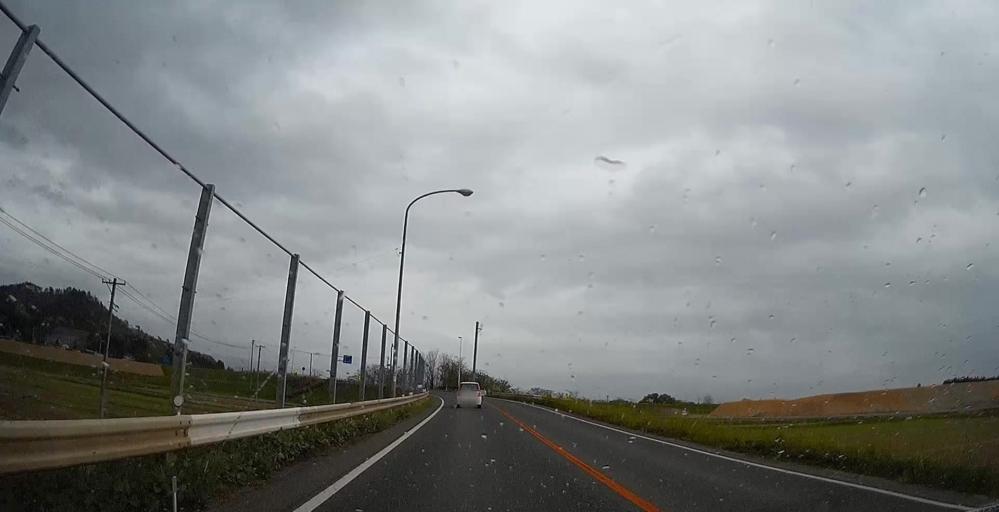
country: JP
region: Yamagata
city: Nagai
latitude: 38.0495
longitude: 140.0723
